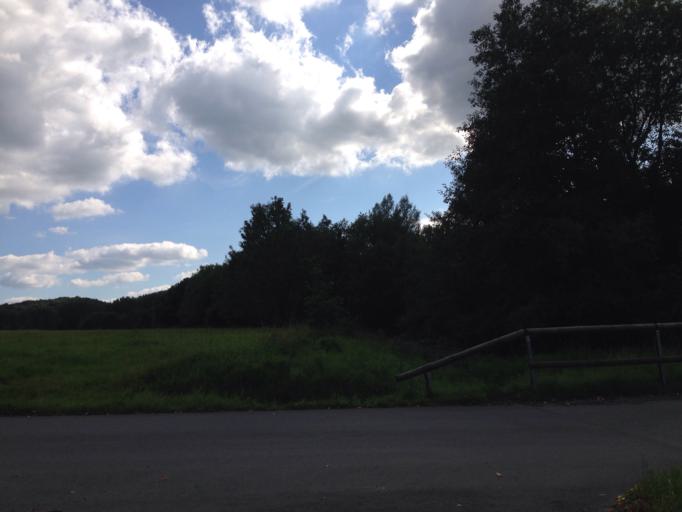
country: DE
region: Hesse
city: Hatzfeld
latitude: 51.0007
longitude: 8.5862
